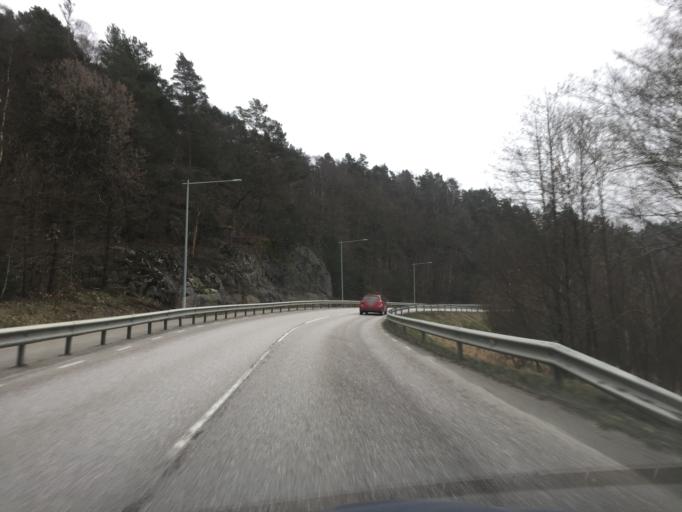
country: SE
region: Vaestra Goetaland
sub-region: Goteborg
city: Rannebergen
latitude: 57.7741
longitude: 12.0737
